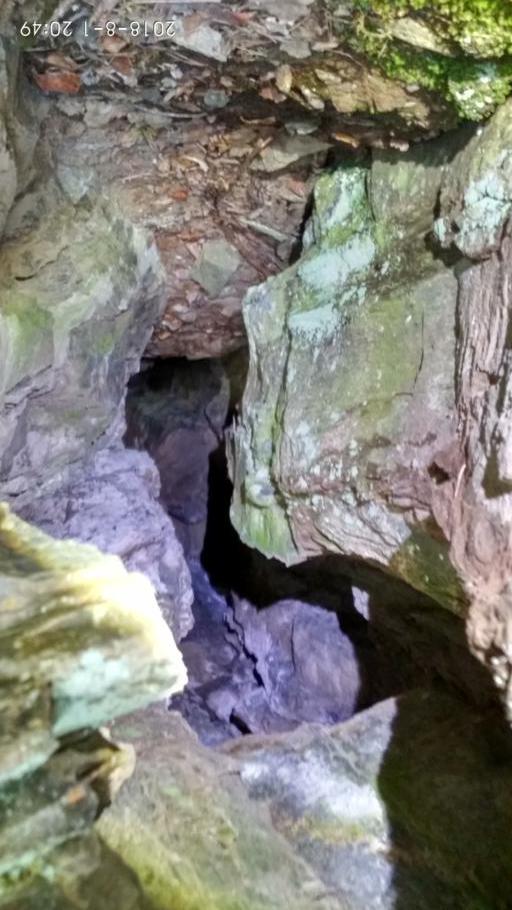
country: NO
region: Oppland
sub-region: Nord-Fron
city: Vinstra
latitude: 61.5950
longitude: 9.7609
